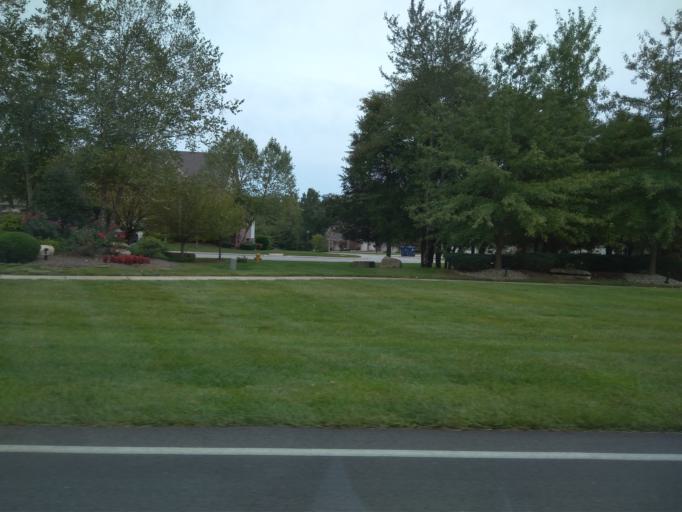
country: US
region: Kentucky
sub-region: Oldham County
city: Pewee Valley
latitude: 38.2813
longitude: -85.4861
